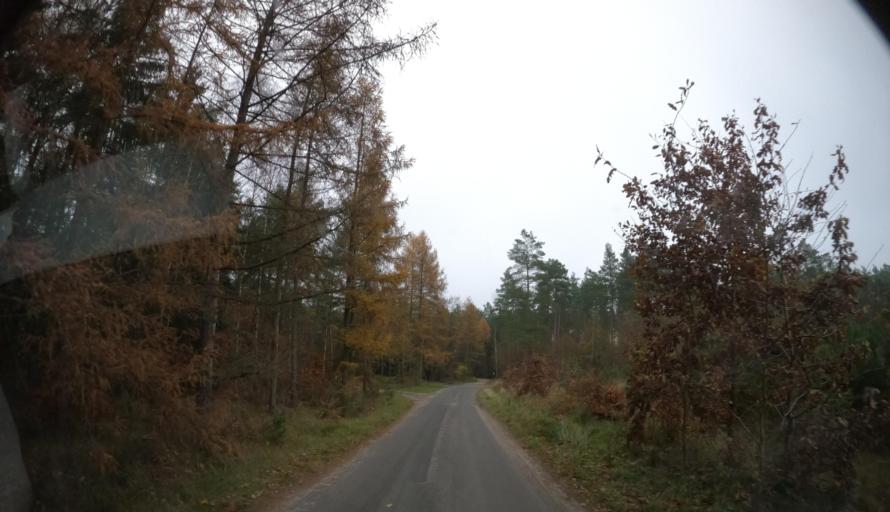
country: PL
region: West Pomeranian Voivodeship
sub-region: Powiat lobeski
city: Radowo Male
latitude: 53.6850
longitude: 15.4576
